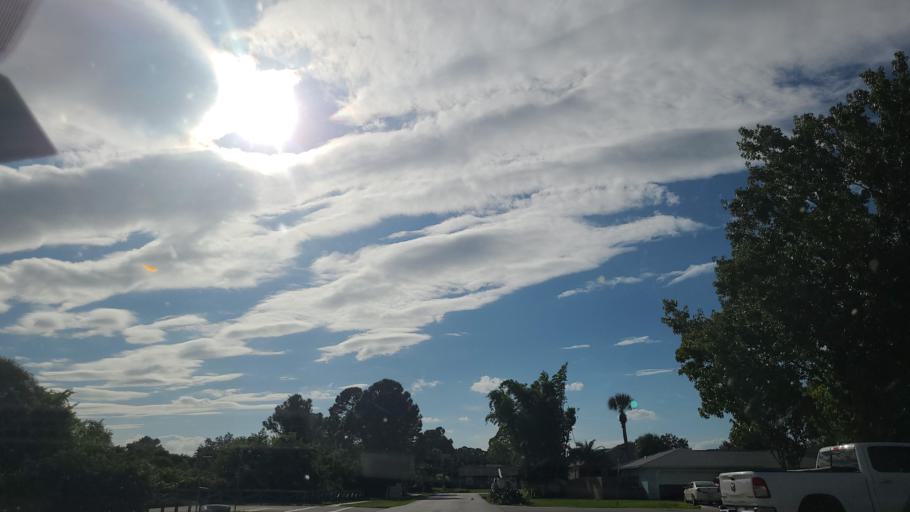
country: US
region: Florida
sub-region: Brevard County
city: Palm Bay
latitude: 27.9806
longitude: -80.6461
